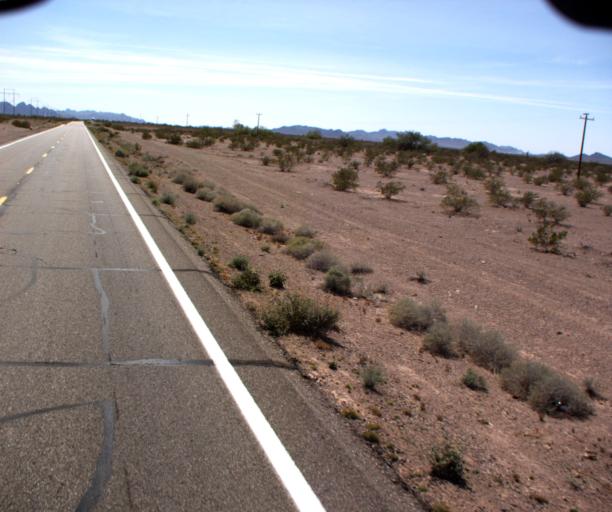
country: US
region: Arizona
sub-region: La Paz County
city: Quartzsite
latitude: 33.4182
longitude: -114.2170
